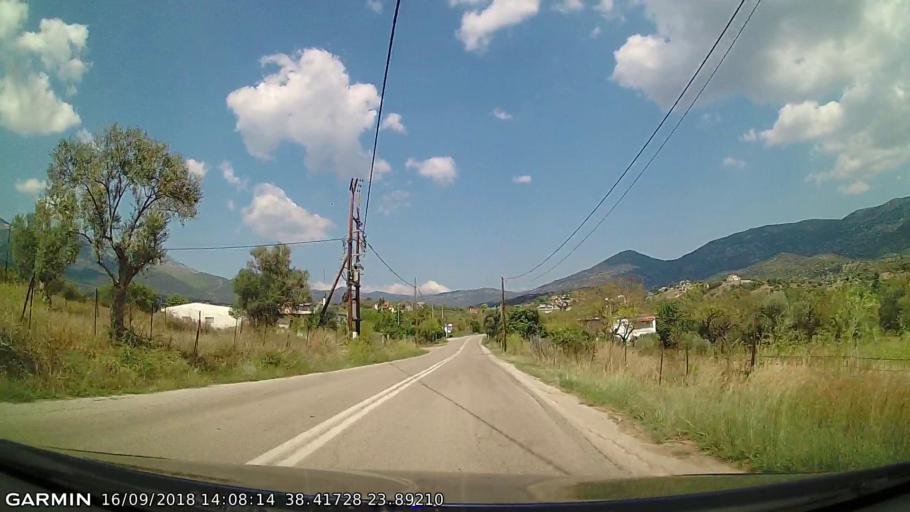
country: GR
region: Central Greece
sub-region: Nomos Evvoias
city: Yimnon
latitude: 38.4173
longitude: 23.8921
